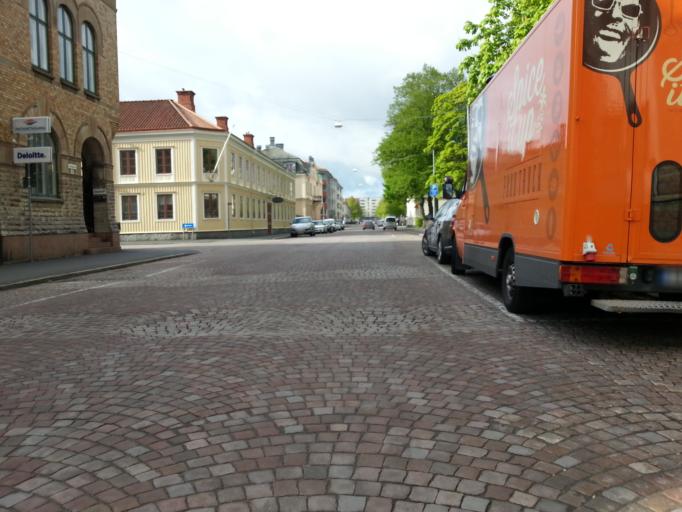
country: SE
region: Joenkoeping
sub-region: Jonkopings Kommun
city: Jonkoping
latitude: 57.7831
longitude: 14.1579
